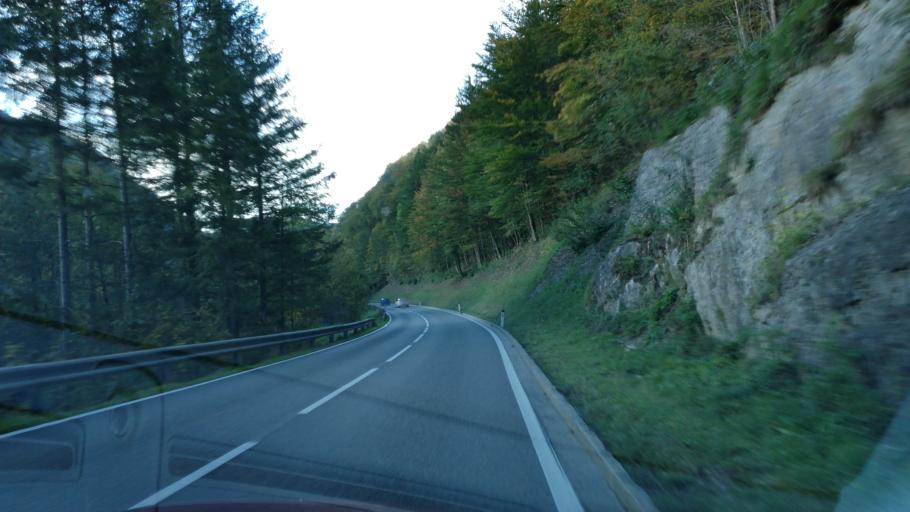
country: AT
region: Upper Austria
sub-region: Politischer Bezirk Steyr-Land
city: Weyer
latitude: 47.8562
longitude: 14.6182
